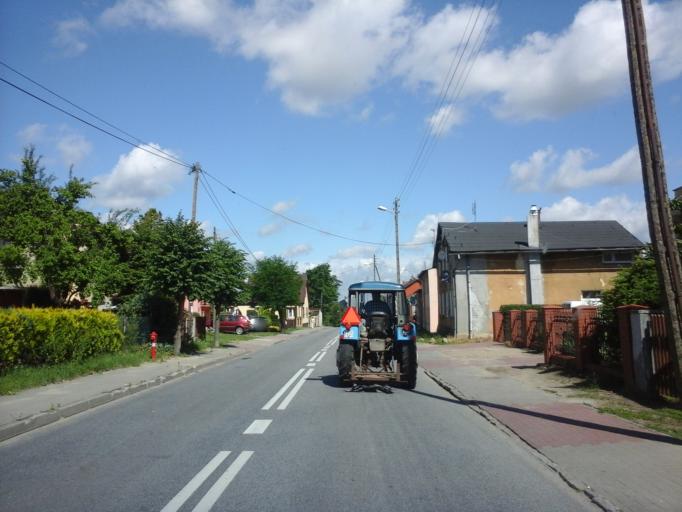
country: PL
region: West Pomeranian Voivodeship
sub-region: Powiat lobeski
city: Wegorzyno
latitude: 53.5329
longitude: 15.5604
